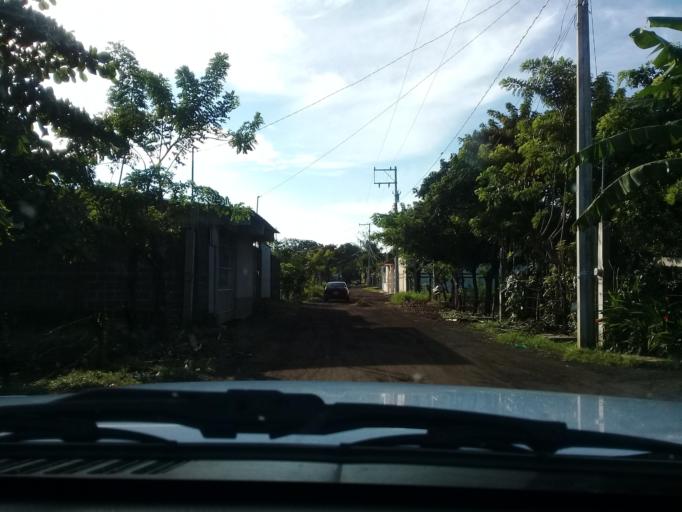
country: MX
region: Veracruz
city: Catemaco
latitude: 18.4305
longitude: -95.1096
